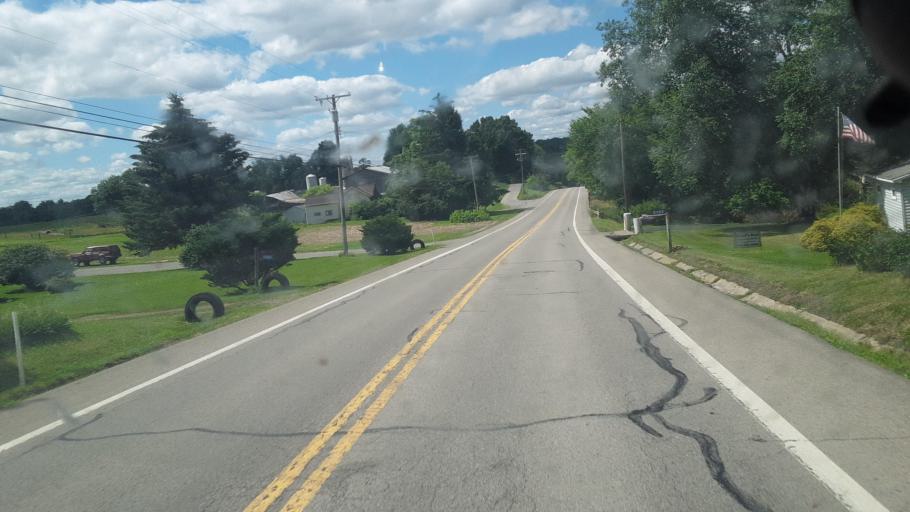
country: US
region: Pennsylvania
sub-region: Butler County
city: Prospect
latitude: 40.9751
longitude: -80.1671
